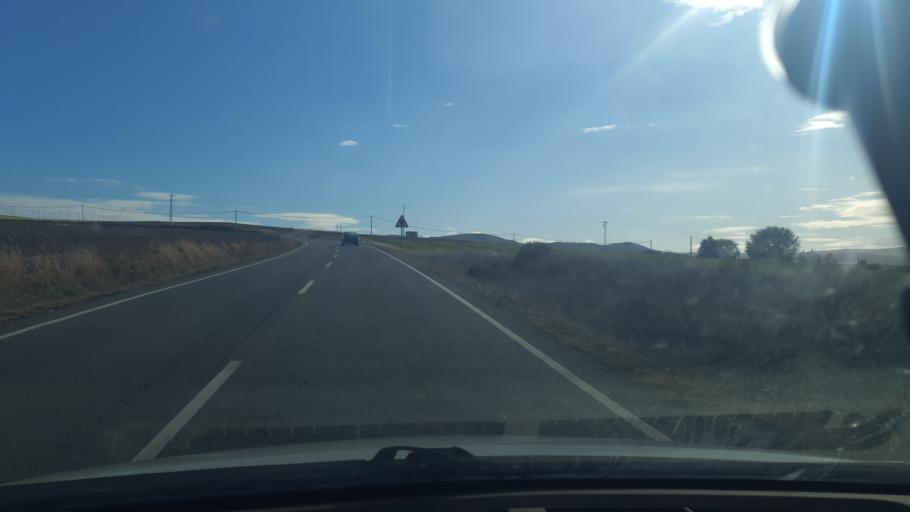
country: ES
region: Castille and Leon
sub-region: Provincia de Avila
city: Penalba de Avila
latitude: 40.7955
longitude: -4.7614
